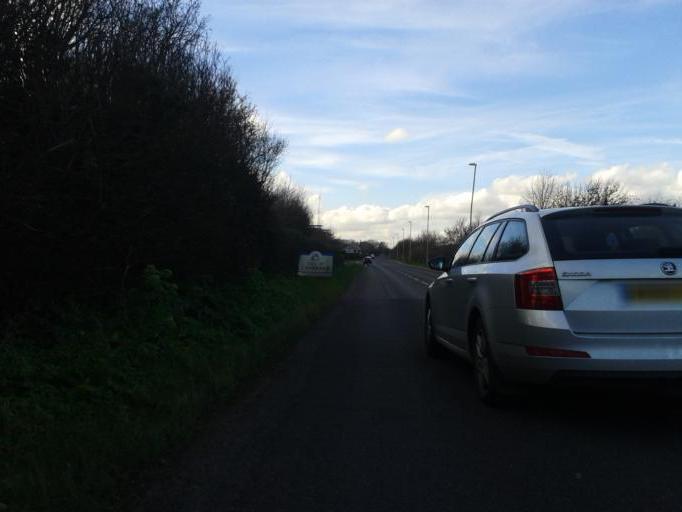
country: GB
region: England
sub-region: Cambridgeshire
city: Fulbourn
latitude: 52.1830
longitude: 0.1815
